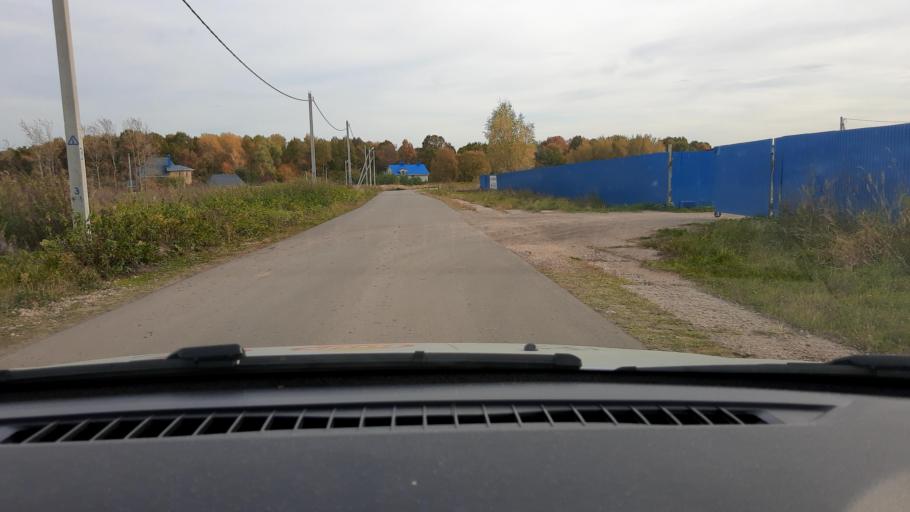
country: RU
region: Nizjnij Novgorod
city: Babino
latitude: 56.1295
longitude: 43.6471
